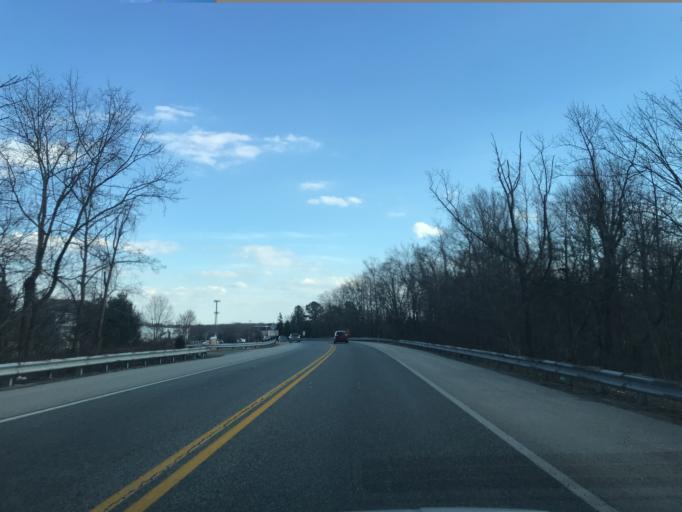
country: US
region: Maryland
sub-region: Cecil County
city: North East
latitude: 39.6435
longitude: -75.9646
